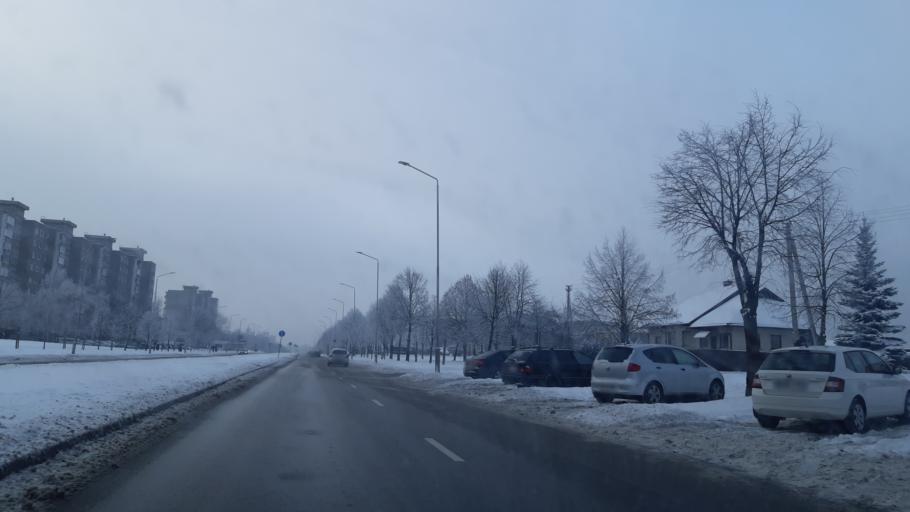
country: LT
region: Kauno apskritis
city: Dainava (Kaunas)
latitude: 54.9309
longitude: 23.9634
